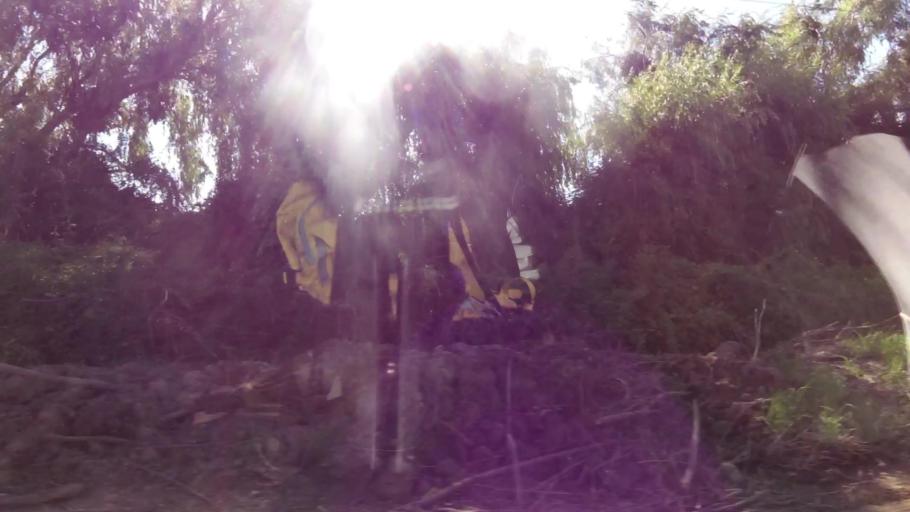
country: CL
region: Maule
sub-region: Provincia de Talca
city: Talca
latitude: -35.4149
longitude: -71.5951
